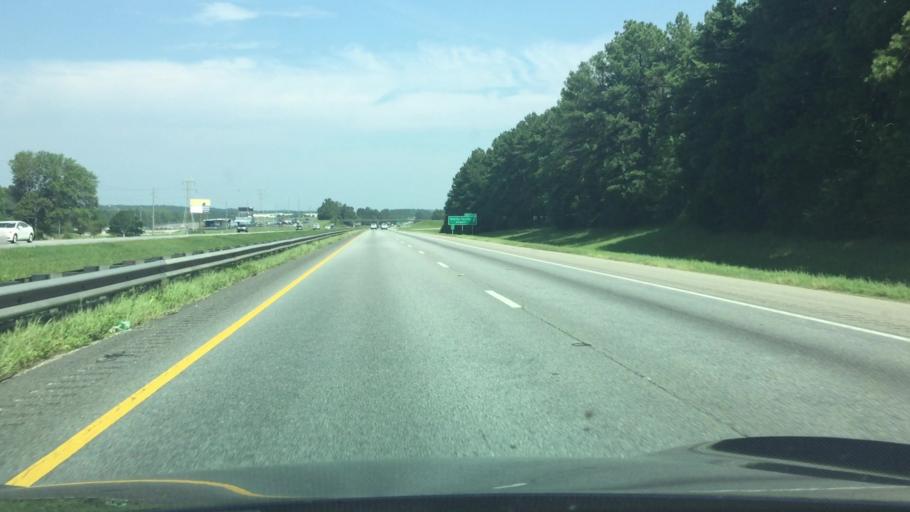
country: US
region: Alabama
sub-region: Shelby County
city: Calera
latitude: 33.1668
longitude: -86.7745
